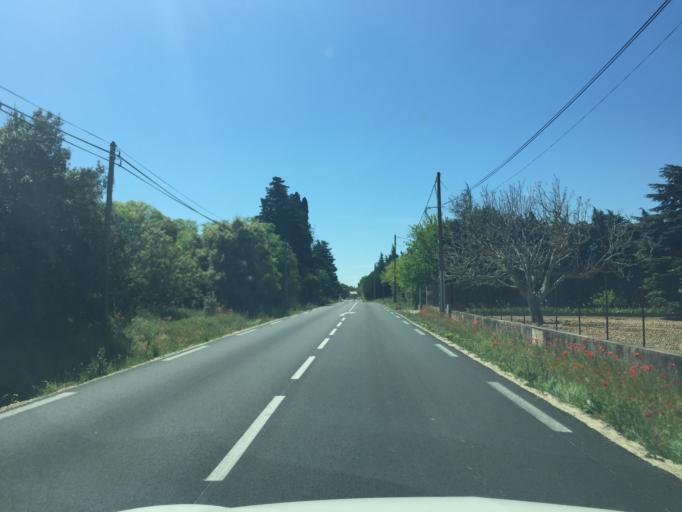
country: FR
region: Provence-Alpes-Cote d'Azur
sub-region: Departement du Vaucluse
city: Orange
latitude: 44.1140
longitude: 4.7946
